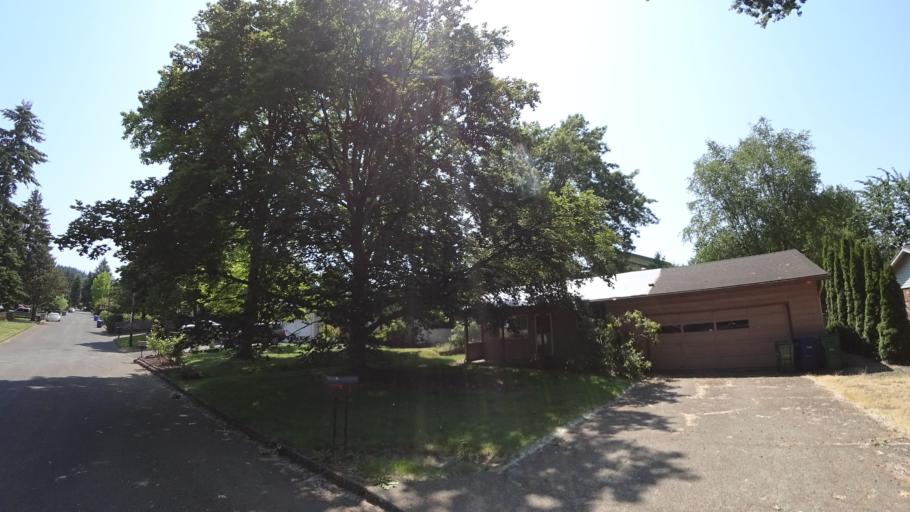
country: US
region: Oregon
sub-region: Clackamas County
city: Clackamas
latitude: 45.4438
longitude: -122.5765
